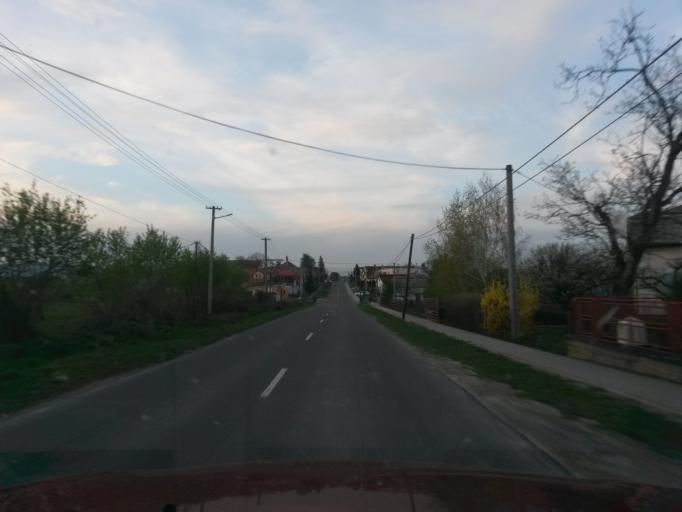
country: SK
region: Kosicky
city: Secovce
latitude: 48.5718
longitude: 21.5672
